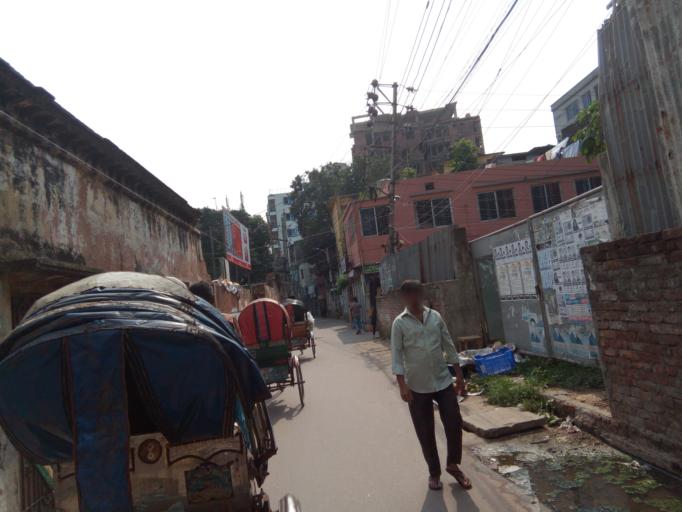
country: BD
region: Dhaka
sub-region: Dhaka
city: Dhaka
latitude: 23.7014
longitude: 90.4218
